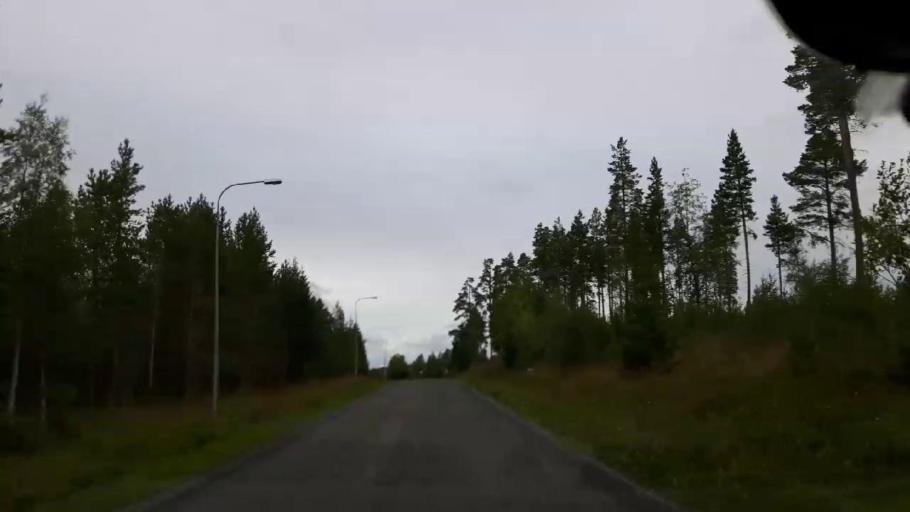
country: SE
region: Jaemtland
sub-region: Krokoms Kommun
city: Krokom
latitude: 63.3133
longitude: 14.3187
